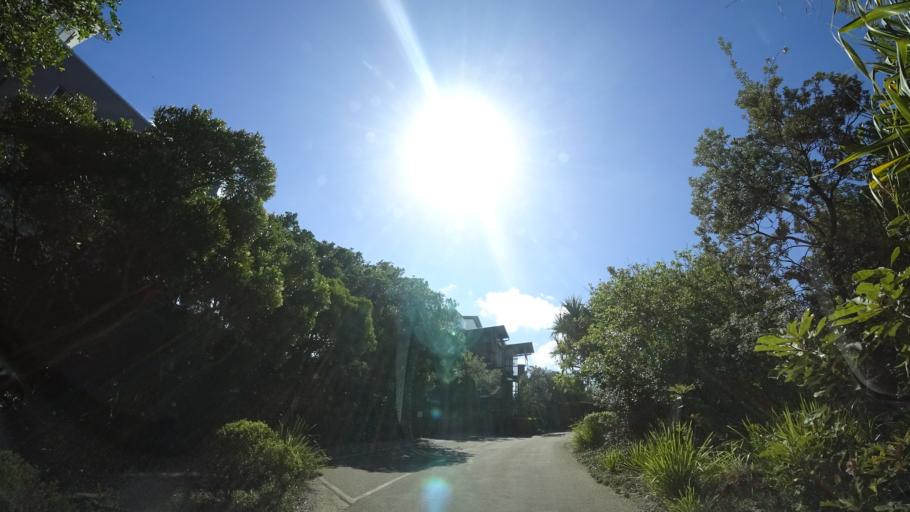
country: AU
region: Queensland
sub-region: Sunshine Coast
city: Mooloolaba
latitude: -26.6362
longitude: 153.1003
